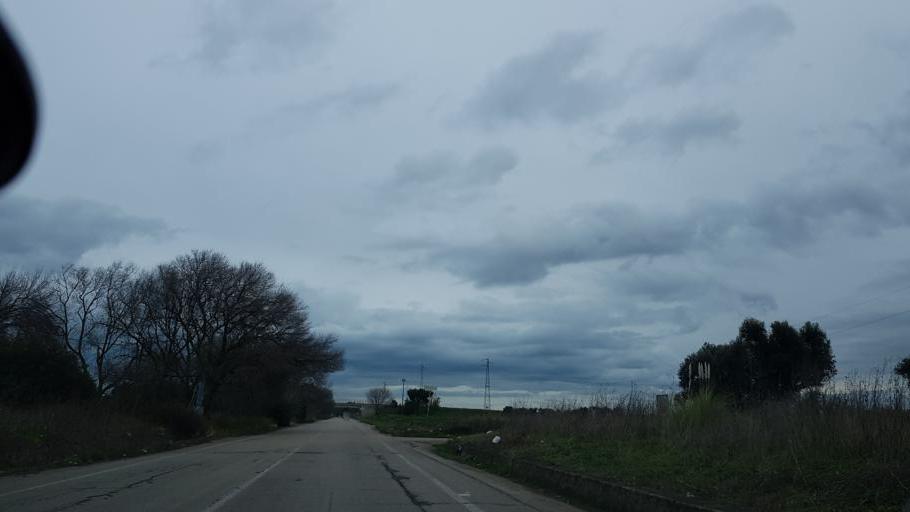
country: IT
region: Apulia
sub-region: Provincia di Brindisi
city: Brindisi
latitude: 40.6189
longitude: 17.9403
